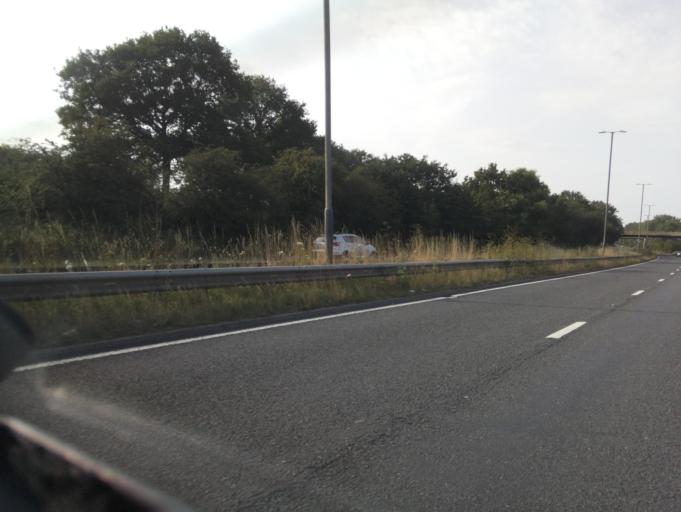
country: GB
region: England
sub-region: Solihull
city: Tidbury Green
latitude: 52.3443
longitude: -1.8760
